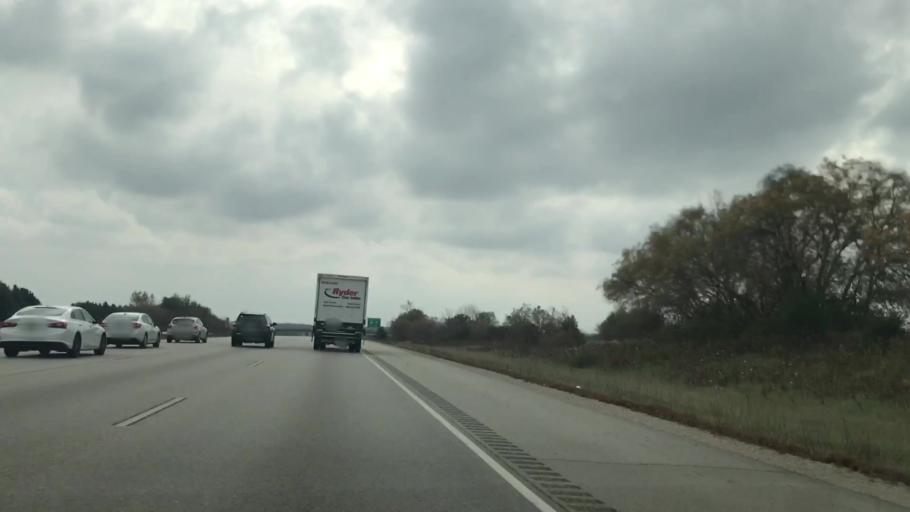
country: US
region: Wisconsin
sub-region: Washington County
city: Richfield
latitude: 43.2252
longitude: -88.1616
